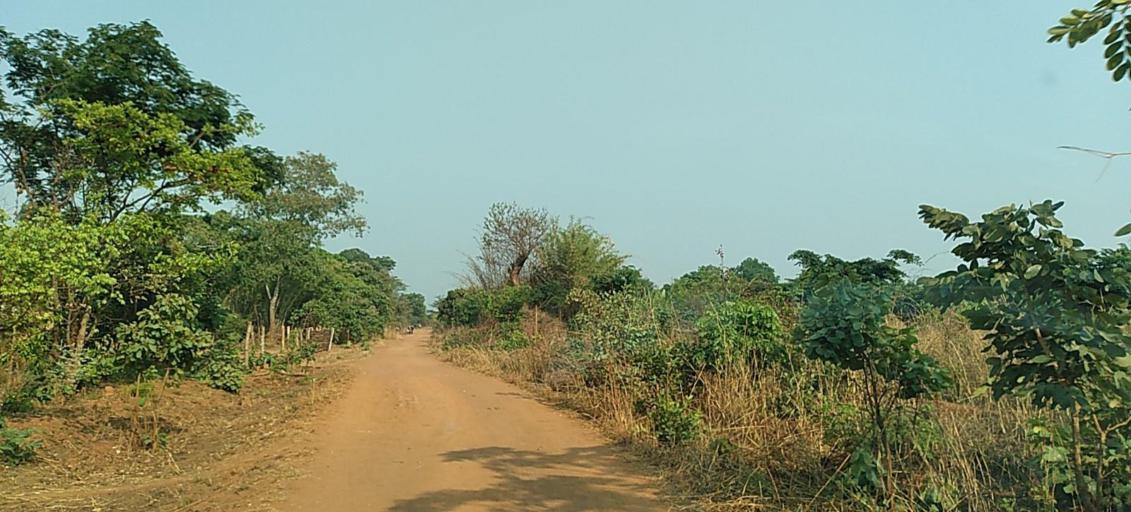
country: ZM
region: Copperbelt
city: Chingola
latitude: -12.8543
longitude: 27.5557
